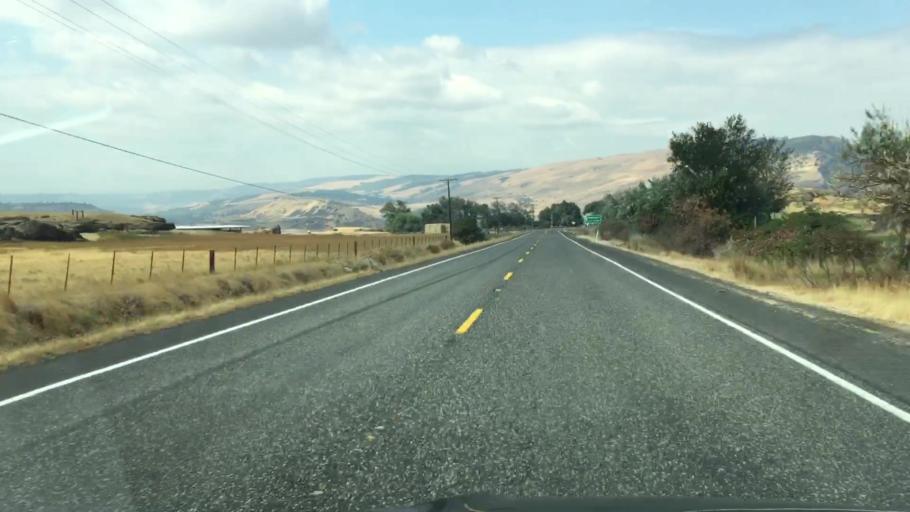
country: US
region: Washington
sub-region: Klickitat County
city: Dallesport
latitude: 45.6485
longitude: -121.1745
